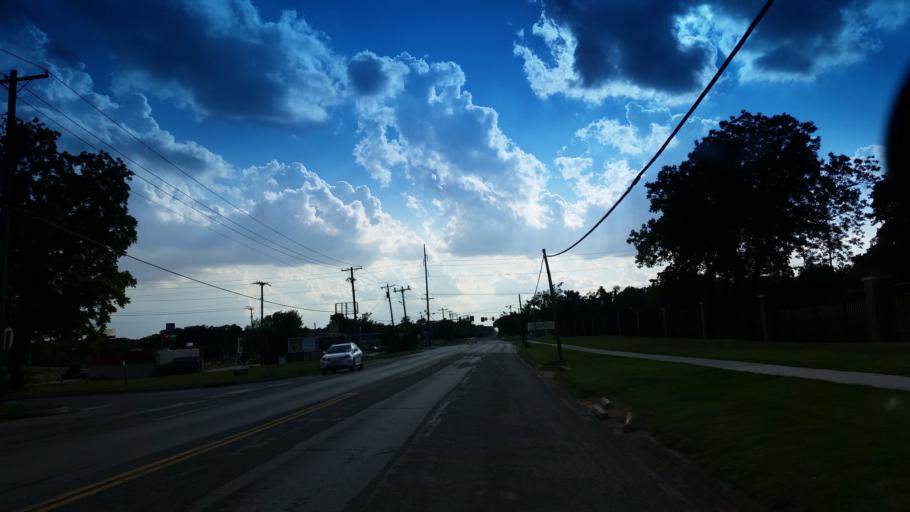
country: US
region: Oklahoma
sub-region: Oklahoma County
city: Nichols Hills
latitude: 35.5368
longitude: -97.4919
